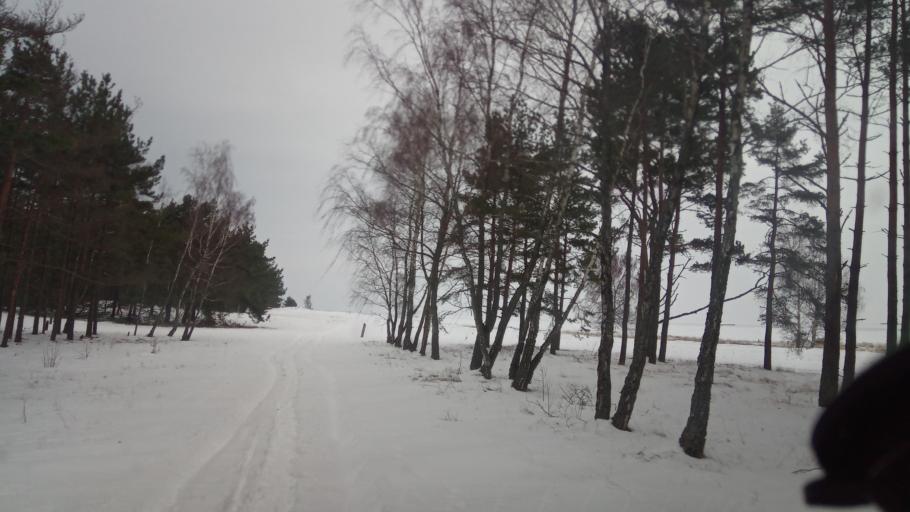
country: LT
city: Neringa
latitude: 55.4219
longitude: 21.1078
